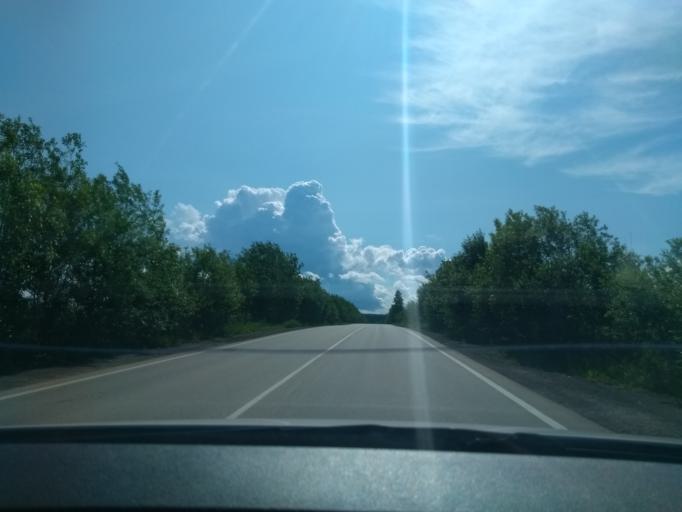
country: RU
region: Perm
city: Bershet'
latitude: 57.8149
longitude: 56.4485
